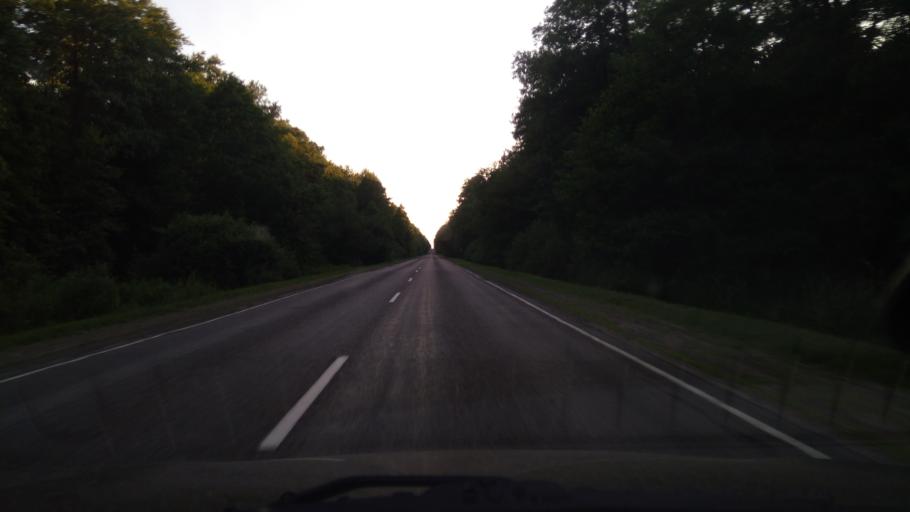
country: BY
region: Brest
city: Nyakhachava
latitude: 52.6108
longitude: 25.1384
